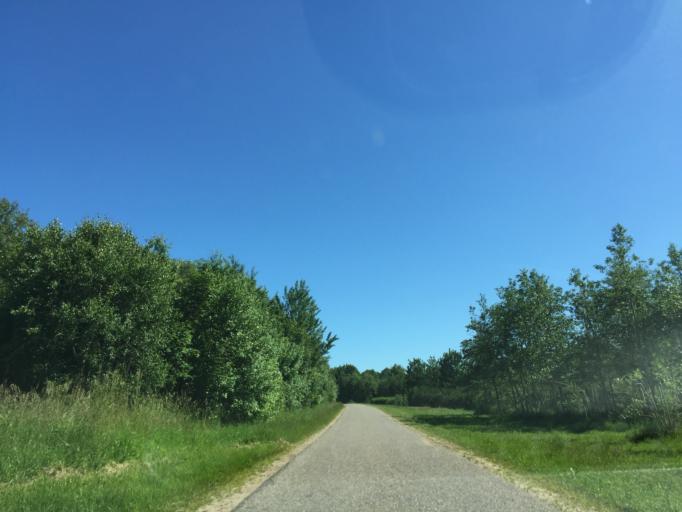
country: DK
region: Central Jutland
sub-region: Viborg Kommune
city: Bjerringbro
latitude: 56.2740
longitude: 9.6876
